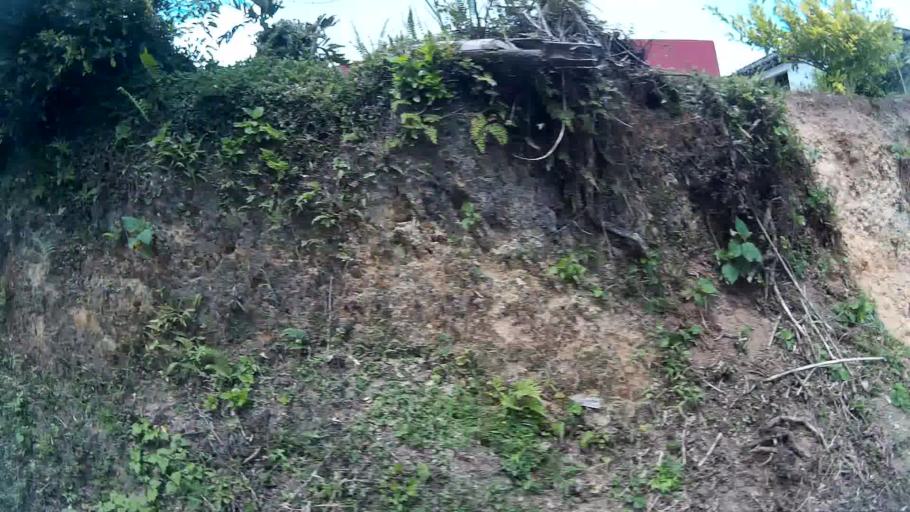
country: CO
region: Caldas
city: Belalcazar
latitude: 4.9785
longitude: -75.8162
